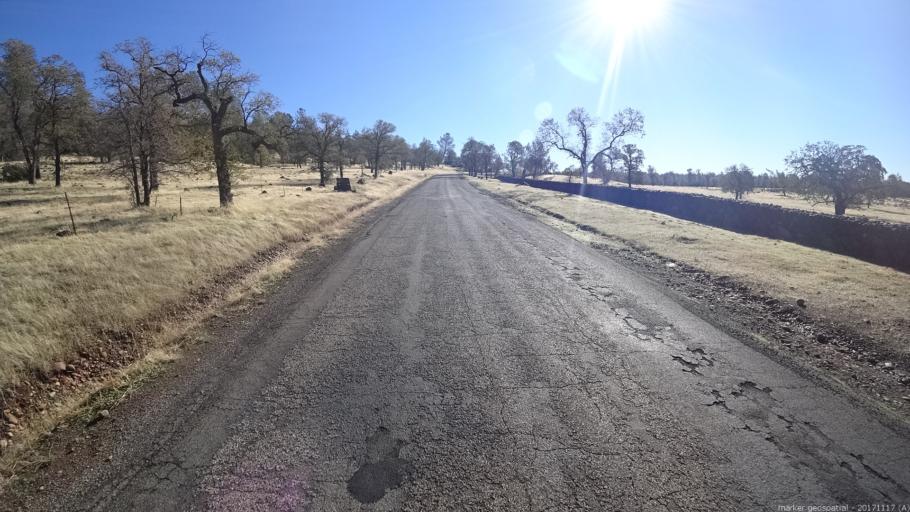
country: US
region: California
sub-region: Shasta County
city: Cottonwood
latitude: 40.4397
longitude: -122.1244
